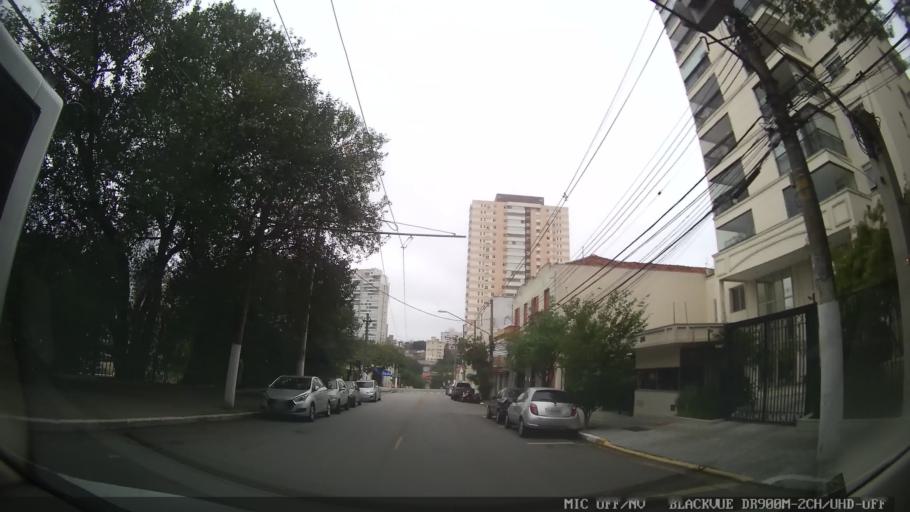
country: BR
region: Sao Paulo
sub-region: Sao Paulo
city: Sao Paulo
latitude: -23.5793
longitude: -46.6332
